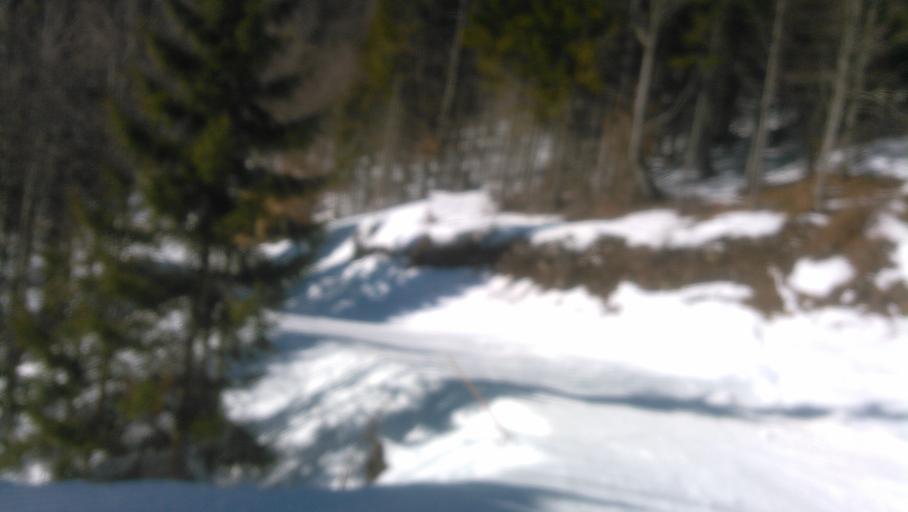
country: SK
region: Banskobystricky
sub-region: Okres Banska Bystrica
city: Brezno
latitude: 48.9275
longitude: 19.5963
